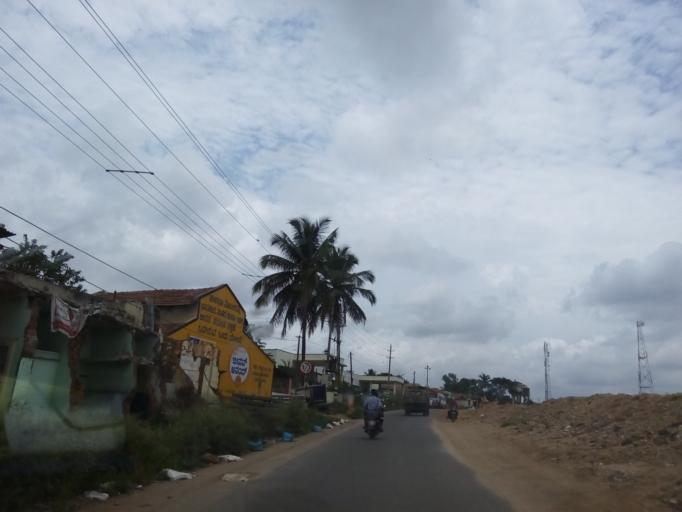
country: IN
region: Karnataka
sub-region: Hassan
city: Hassan
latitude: 12.9838
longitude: 76.2174
